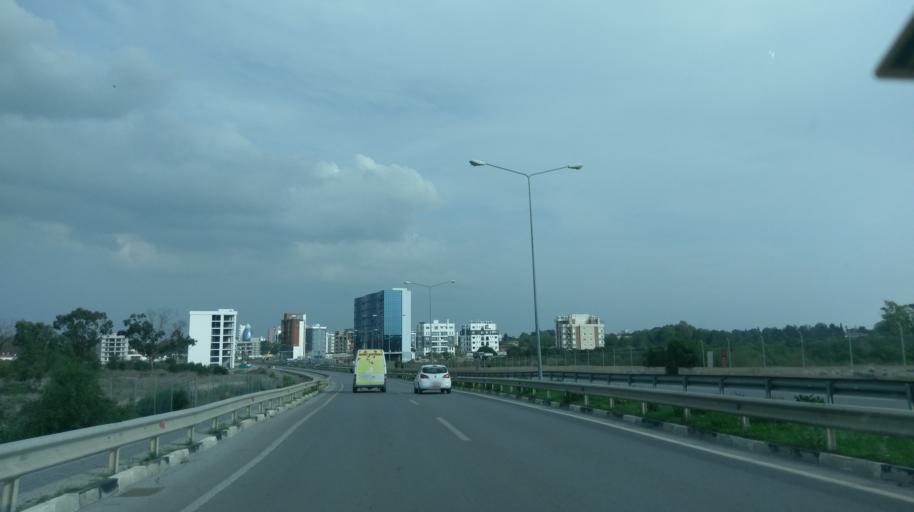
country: CY
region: Lefkosia
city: Nicosia
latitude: 35.1897
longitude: 33.3388
